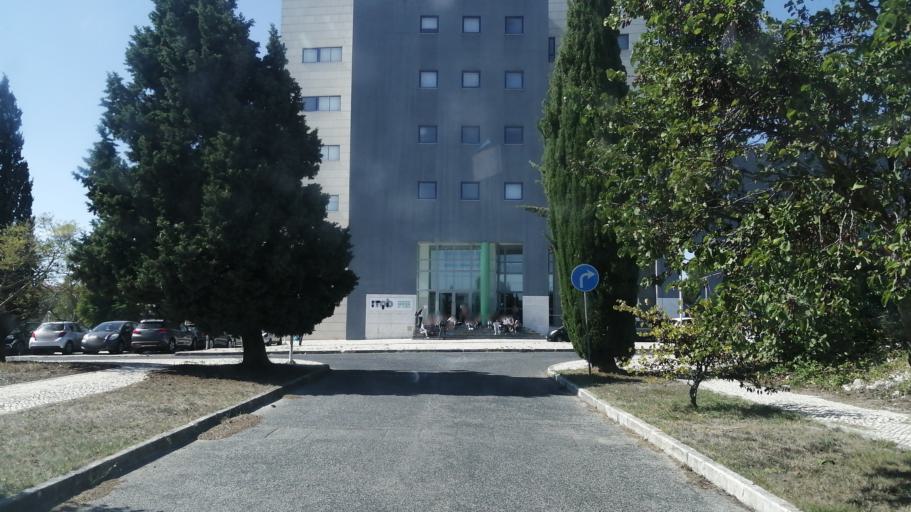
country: PT
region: Lisbon
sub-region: Oeiras
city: Carcavelos
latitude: 38.6958
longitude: -9.3206
